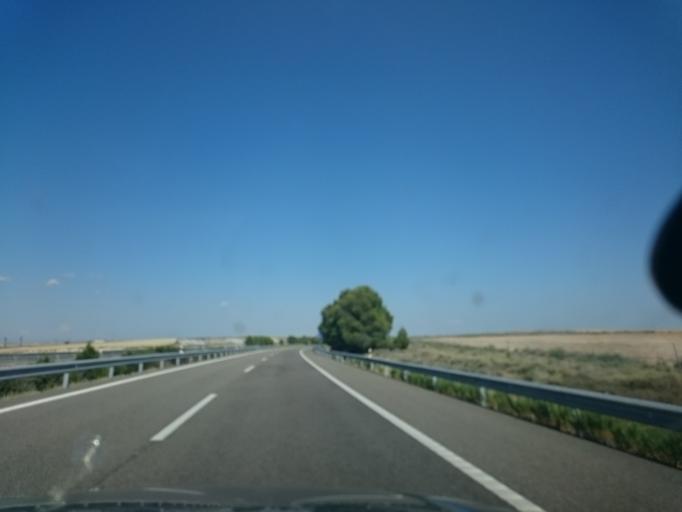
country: ES
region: Aragon
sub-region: Provincia de Zaragoza
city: Bujaraloz
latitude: 41.5259
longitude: -0.1943
